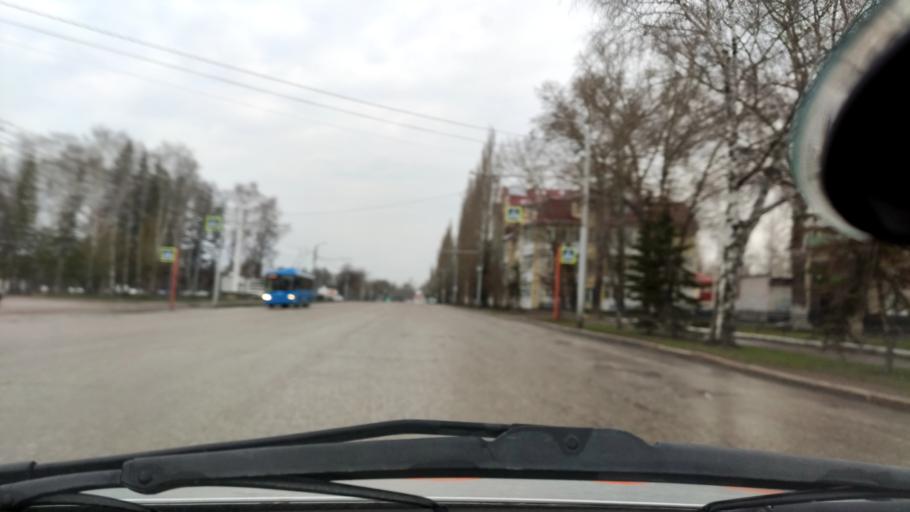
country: RU
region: Bashkortostan
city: Sterlitamak
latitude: 53.6502
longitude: 55.9460
